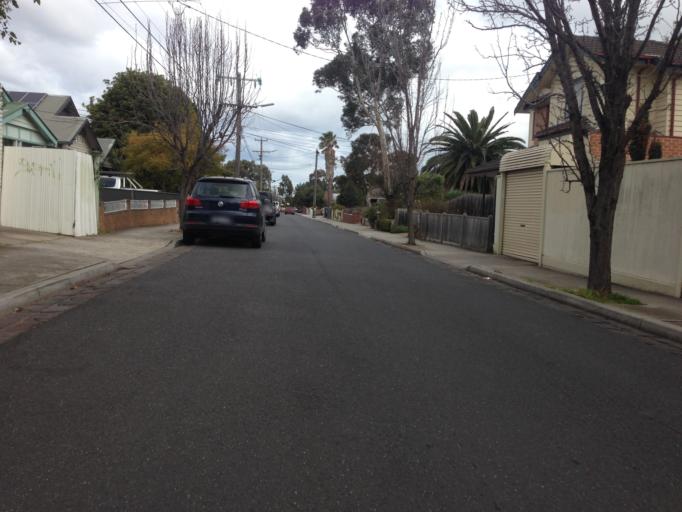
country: AU
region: Victoria
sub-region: Darebin
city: Northcote
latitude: -37.7729
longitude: 145.0051
